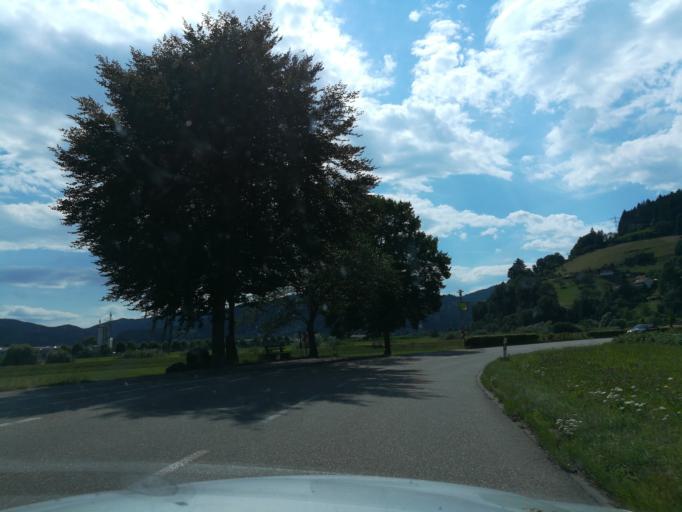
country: DE
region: Baden-Wuerttemberg
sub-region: Freiburg Region
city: Fischerbach
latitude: 48.2837
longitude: 8.1029
